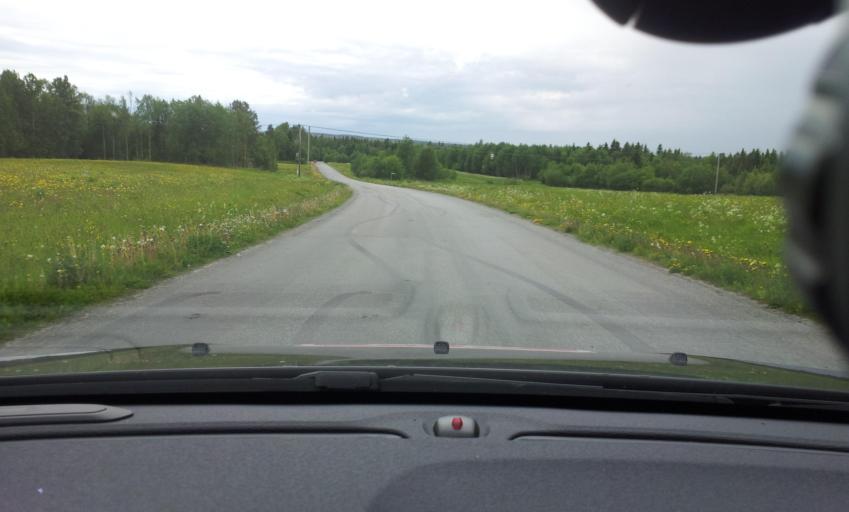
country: SE
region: Jaemtland
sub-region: OEstersunds Kommun
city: Brunflo
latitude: 63.0774
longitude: 14.8634
